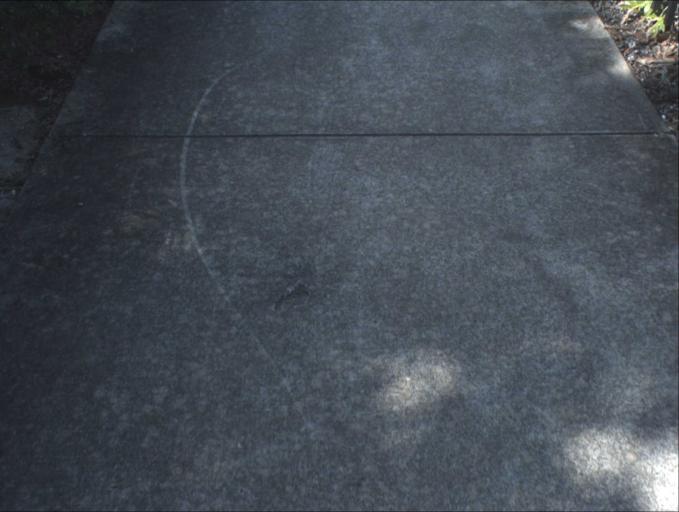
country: AU
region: Queensland
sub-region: Logan
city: Waterford West
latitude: -27.6967
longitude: 153.1538
